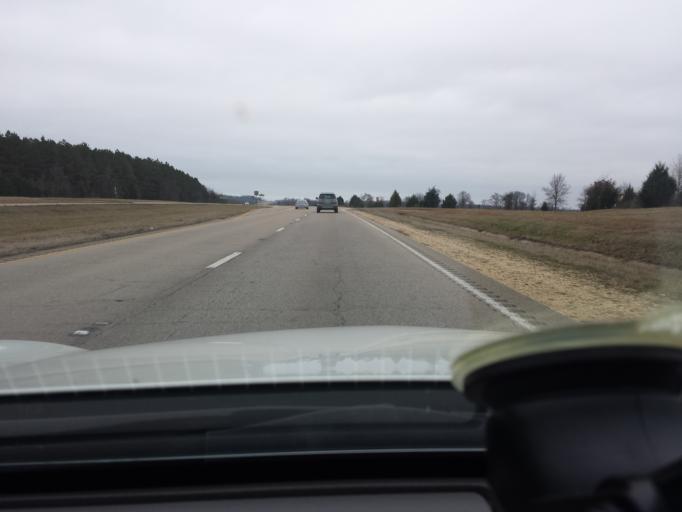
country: US
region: Mississippi
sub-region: Lee County
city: Shannon
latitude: 34.0698
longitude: -88.7036
